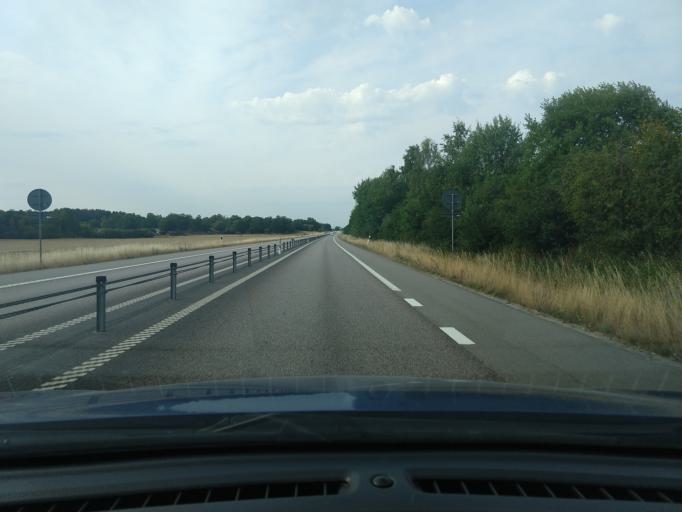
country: SE
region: Blekinge
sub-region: Ronneby Kommun
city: Kallinge
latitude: 56.2396
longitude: 15.2547
